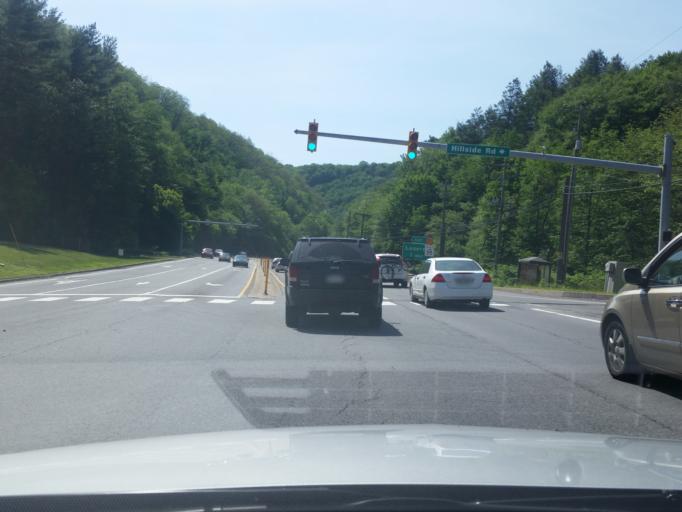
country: US
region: Pennsylvania
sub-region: Luzerne County
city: Trucksville
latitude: 41.2961
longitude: -75.9244
